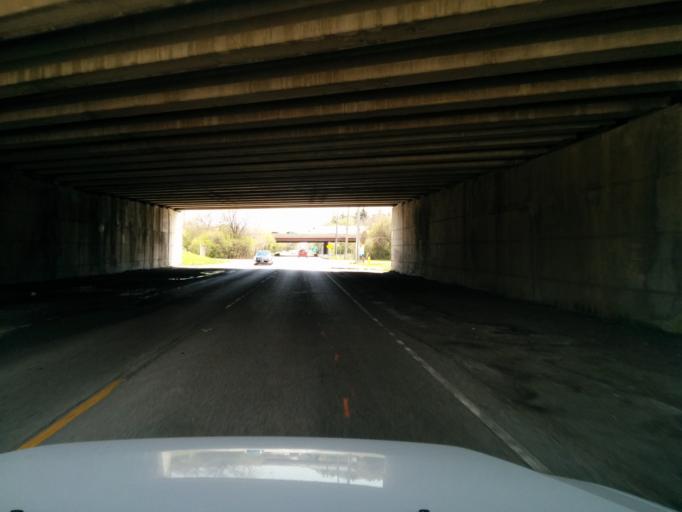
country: US
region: Illinois
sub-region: Cook County
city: Indian Head Park
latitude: 41.7625
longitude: -87.8967
